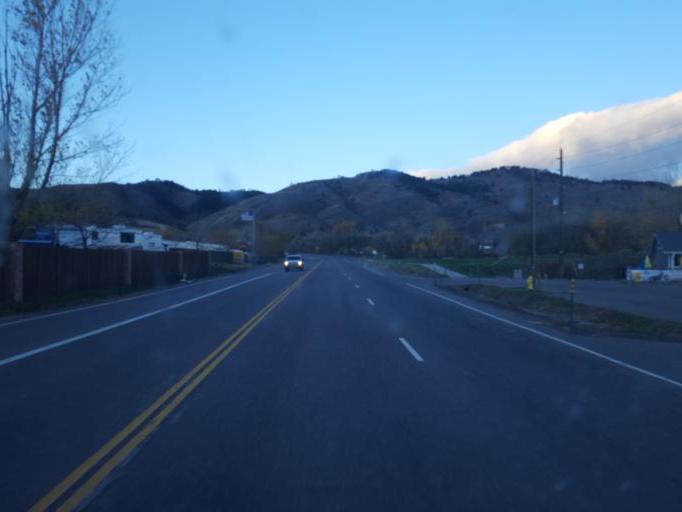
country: US
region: Colorado
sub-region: Jefferson County
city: West Pleasant View
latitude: 39.7201
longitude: -105.2015
